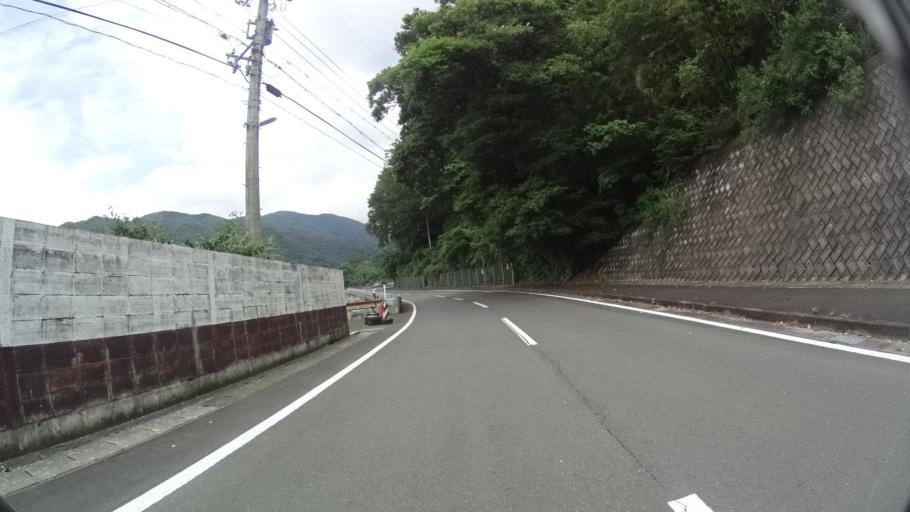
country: JP
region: Kyoto
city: Maizuru
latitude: 35.5212
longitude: 135.3449
